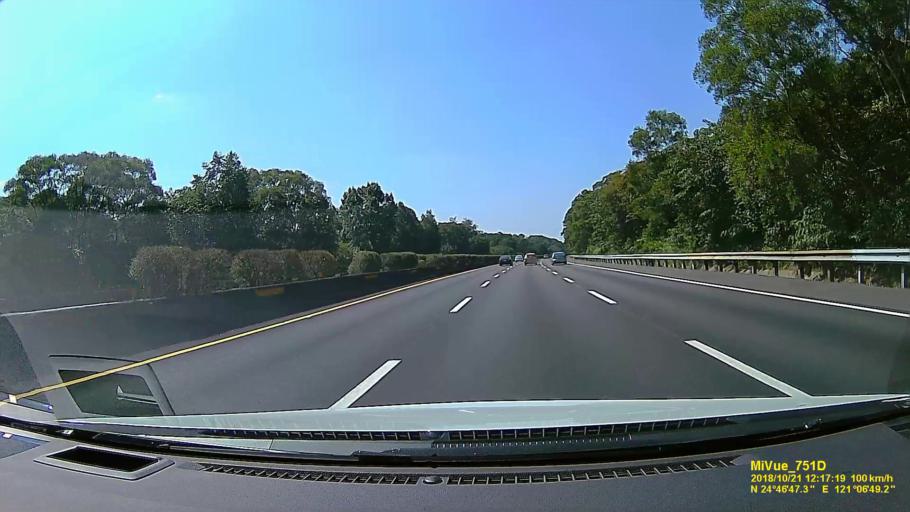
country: TW
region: Taiwan
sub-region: Hsinchu
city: Zhubei
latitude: 24.7798
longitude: 121.1129
